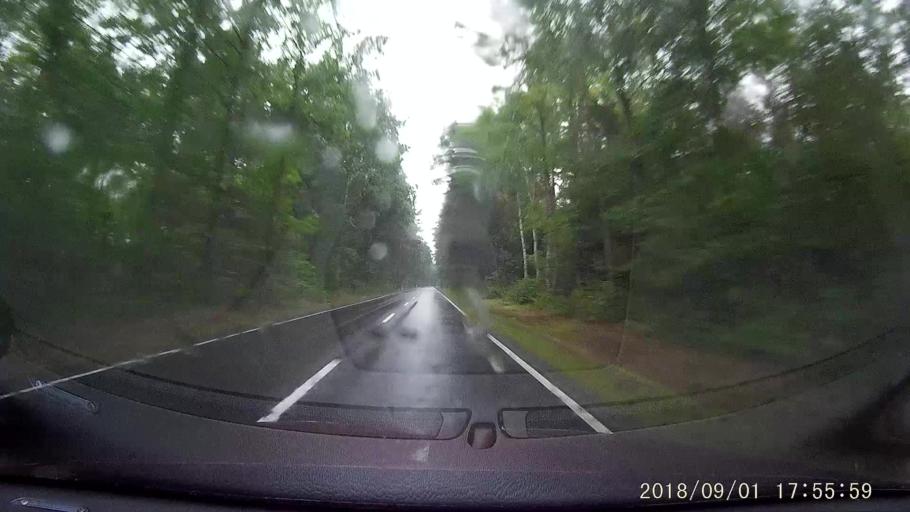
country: PL
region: Lubusz
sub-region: Powiat zaganski
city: Ilowa
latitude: 51.4538
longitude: 15.1996
